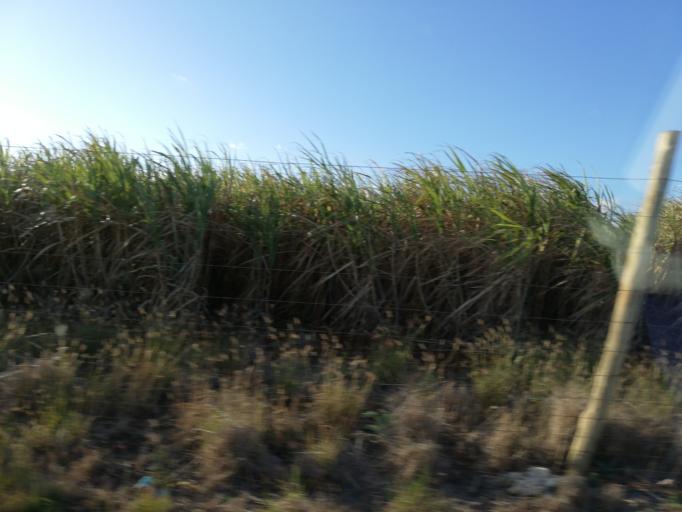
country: MU
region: Pamplemousses
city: Arsenal
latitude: -20.0803
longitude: 57.5322
